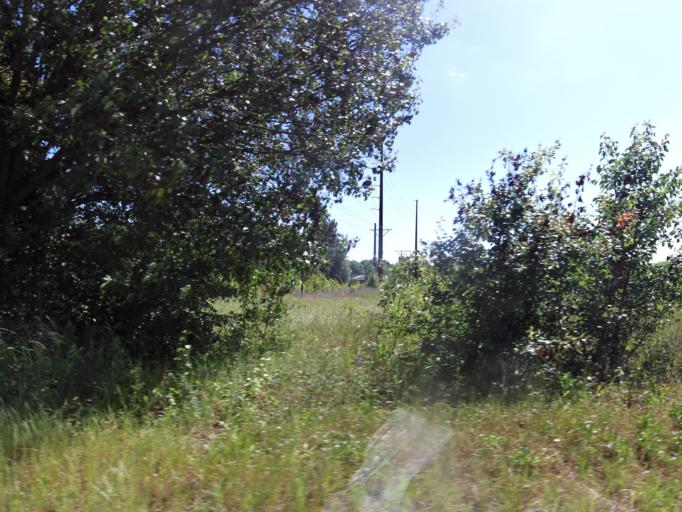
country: US
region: South Carolina
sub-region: Aiken County
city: Aiken
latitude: 33.5505
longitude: -81.6891
